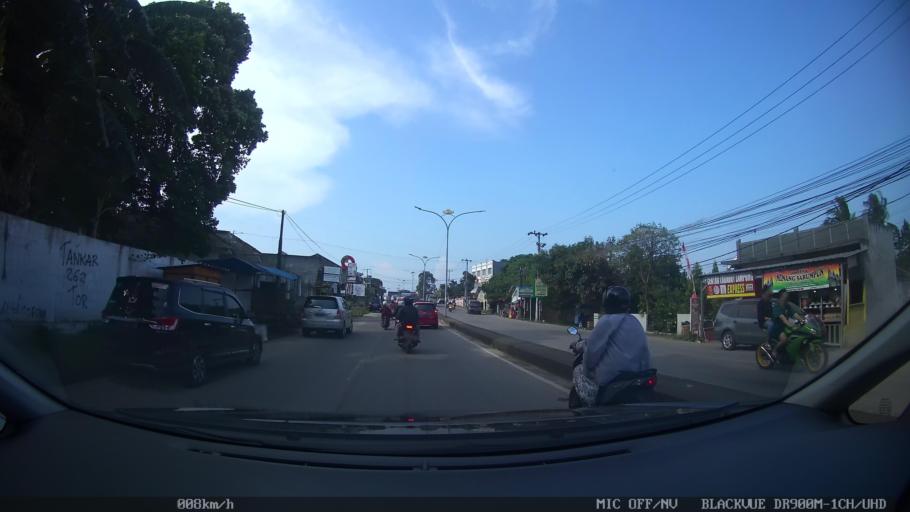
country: ID
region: Lampung
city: Kedaton
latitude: -5.3722
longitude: 105.2271
